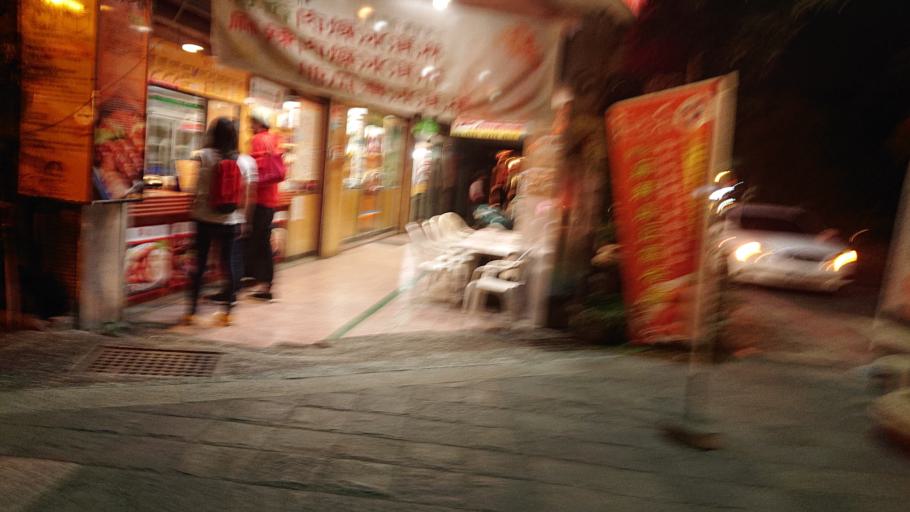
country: TW
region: Taiwan
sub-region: Tainan
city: Tainan
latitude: 22.9902
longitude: 120.2049
